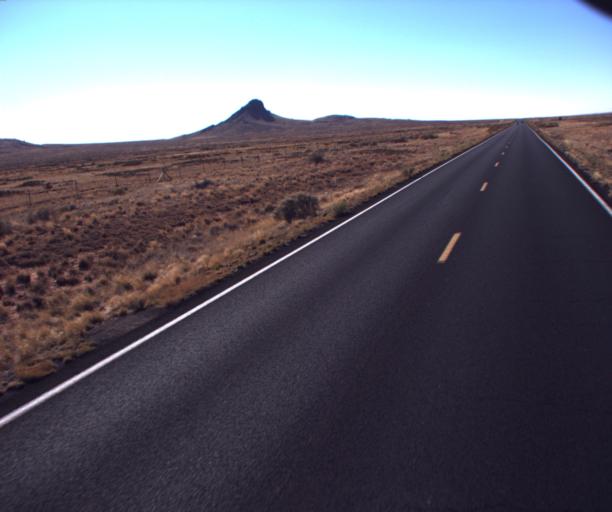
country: US
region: Arizona
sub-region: Navajo County
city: Dilkon
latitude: 35.4367
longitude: -110.4249
